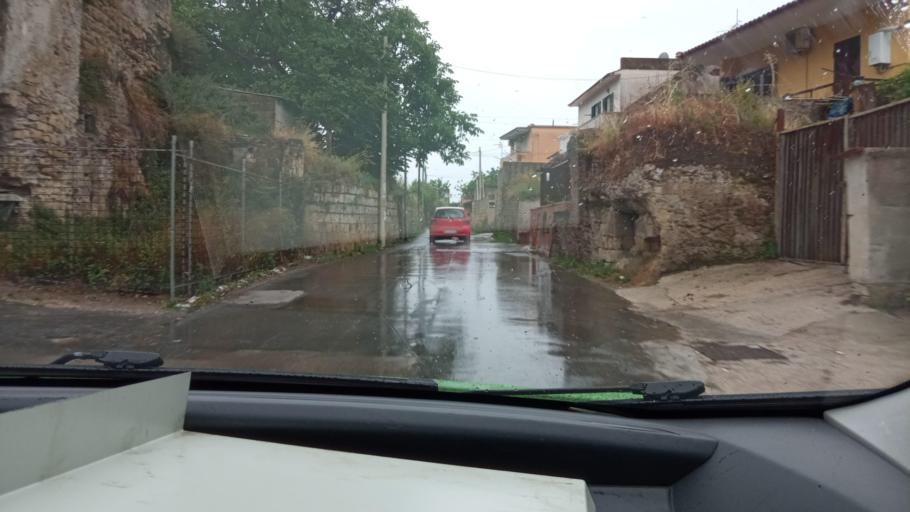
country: IT
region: Campania
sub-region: Provincia di Napoli
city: Quarto
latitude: 40.8445
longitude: 14.1188
